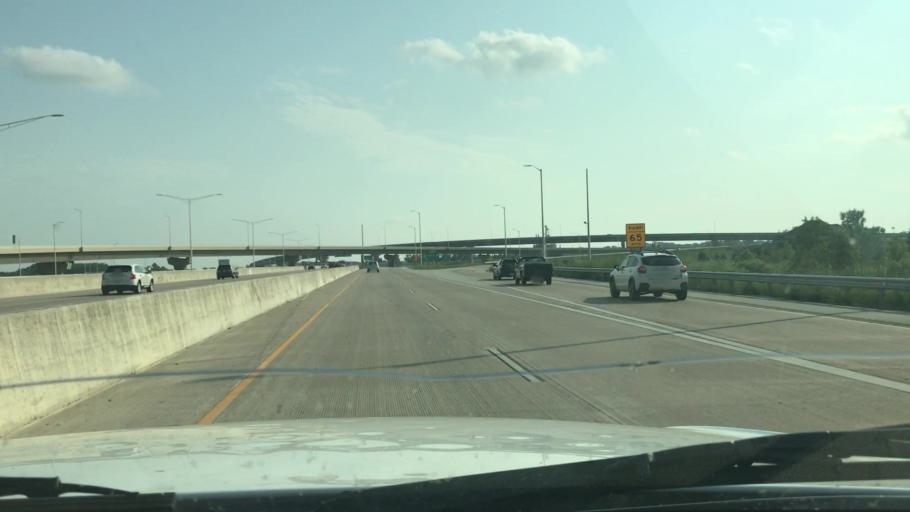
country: US
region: Wisconsin
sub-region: Brown County
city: Howard
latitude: 44.5428
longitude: -88.0739
